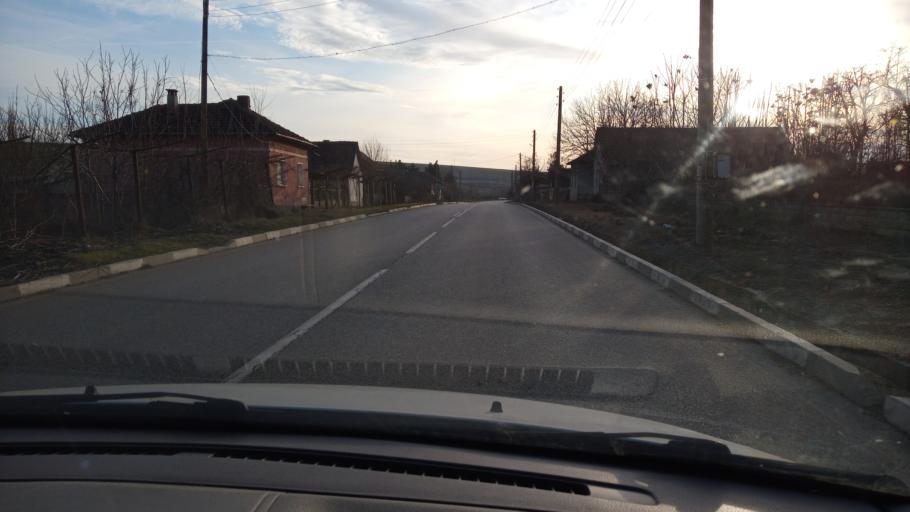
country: BG
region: Pleven
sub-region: Obshtina Pleven
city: Slavyanovo
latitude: 43.5502
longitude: 24.8632
